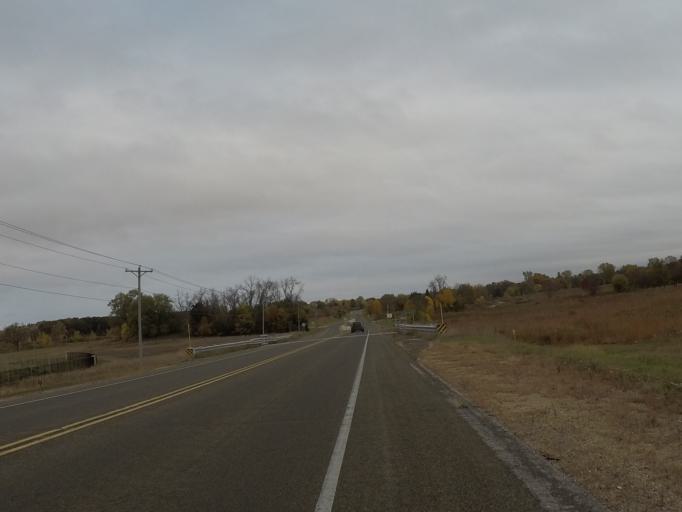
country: US
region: Wisconsin
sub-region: Dane County
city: Shorewood Hills
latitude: 43.1350
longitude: -89.4420
